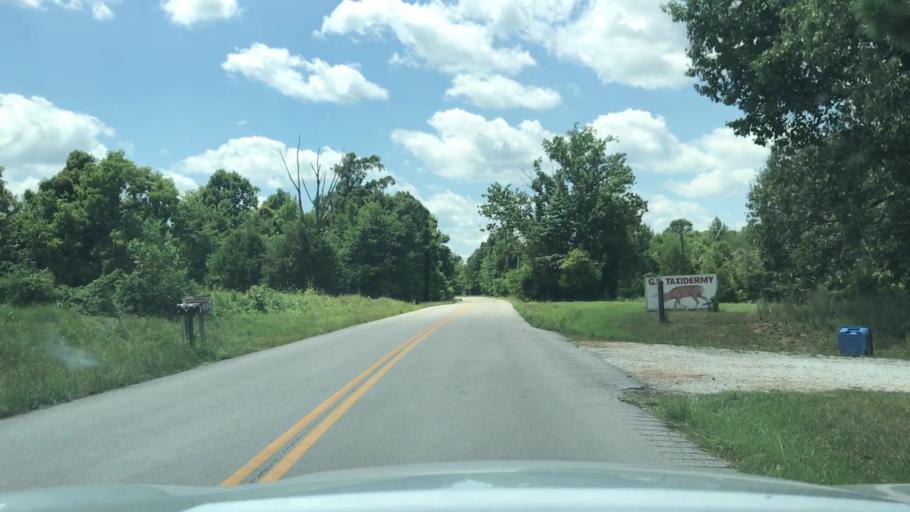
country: US
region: Kentucky
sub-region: Hopkins County
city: Nortonville
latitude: 37.1142
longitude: -87.3279
